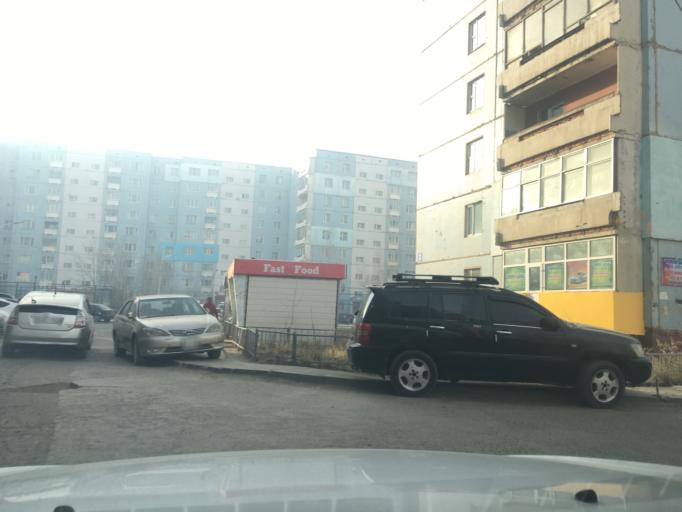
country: MN
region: Ulaanbaatar
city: Ulaanbaatar
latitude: 47.9152
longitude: 106.8635
